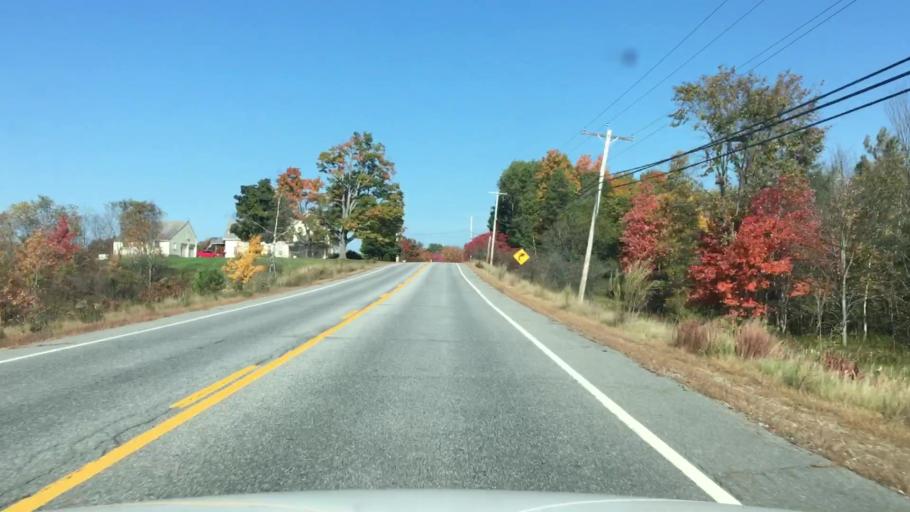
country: US
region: Maine
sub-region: Sagadahoc County
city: Topsham
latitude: 43.9760
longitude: -69.9597
